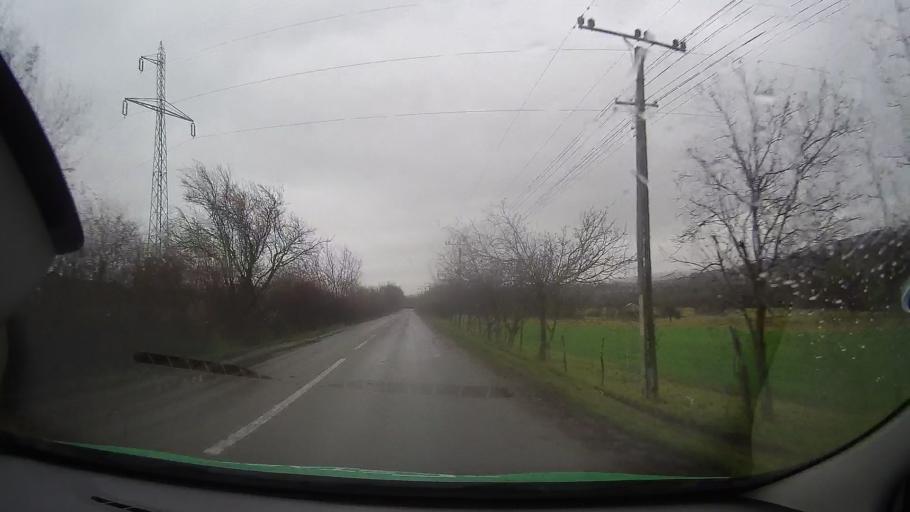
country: RO
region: Mures
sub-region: Comuna Brancovenesti
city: Valenii de Mures
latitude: 46.9225
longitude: 24.7742
